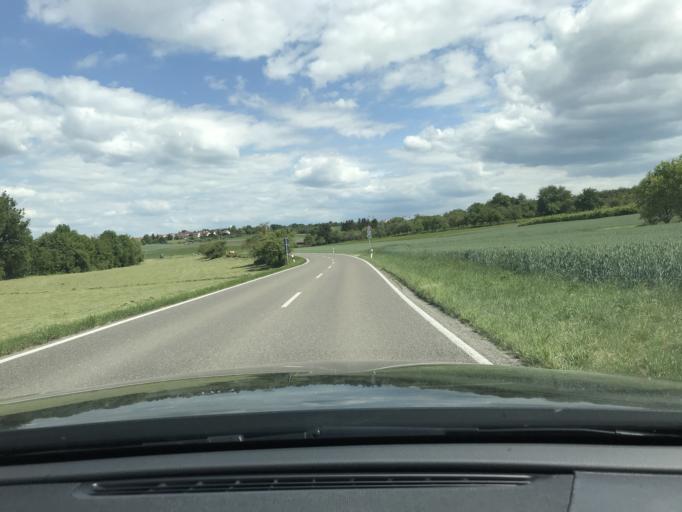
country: DE
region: Baden-Wuerttemberg
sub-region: Regierungsbezirk Stuttgart
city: Schwaikheim
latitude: 48.8726
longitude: 9.3306
